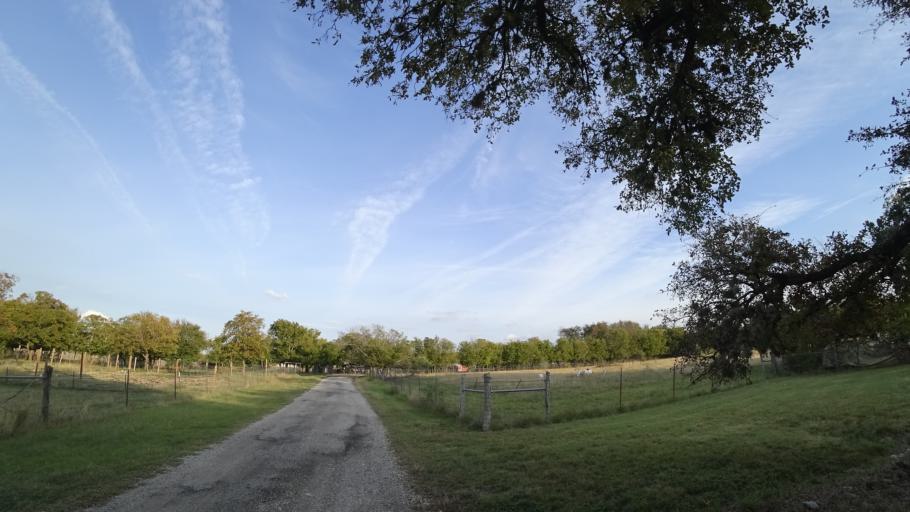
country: US
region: Texas
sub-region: Williamson County
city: Round Rock
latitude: 30.5056
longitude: -97.6682
